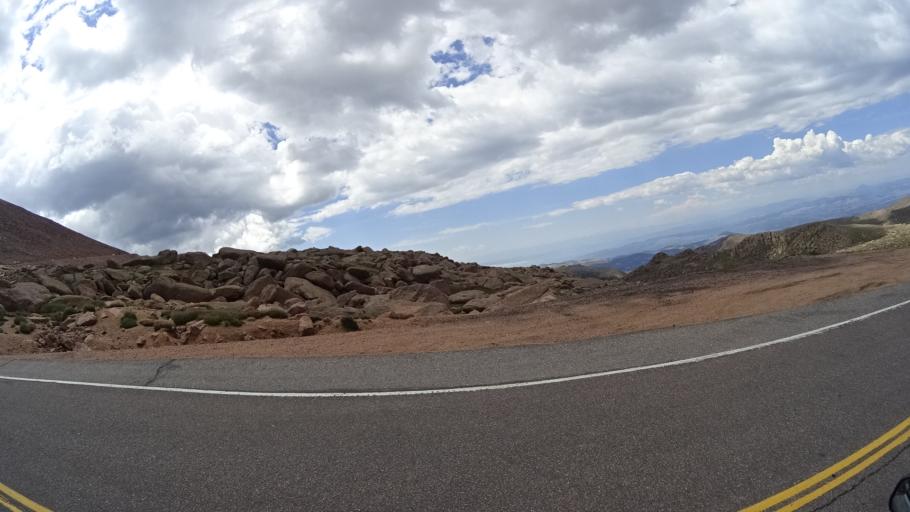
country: US
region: Colorado
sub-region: El Paso County
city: Cascade-Chipita Park
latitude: 38.8457
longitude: -105.0530
